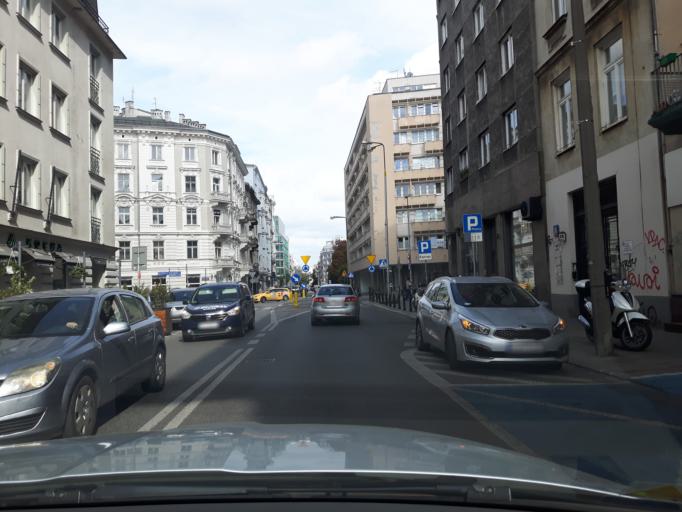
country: PL
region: Masovian Voivodeship
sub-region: Warszawa
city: Srodmiescie
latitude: 52.2217
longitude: 21.0191
